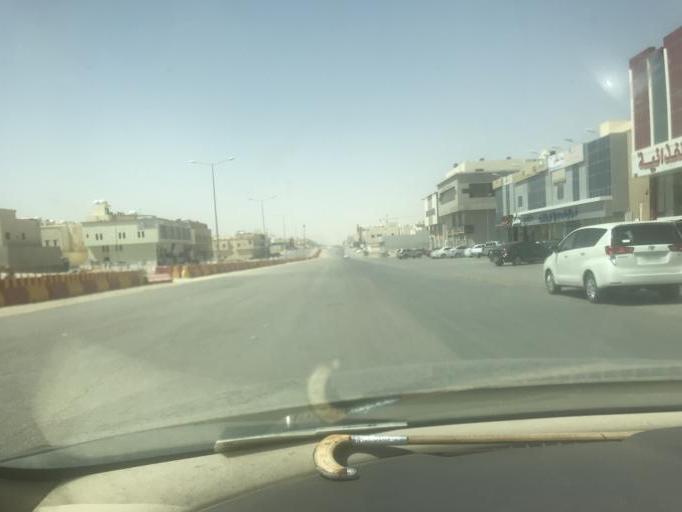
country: SA
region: Ar Riyad
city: Riyadh
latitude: 24.8132
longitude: 46.5992
